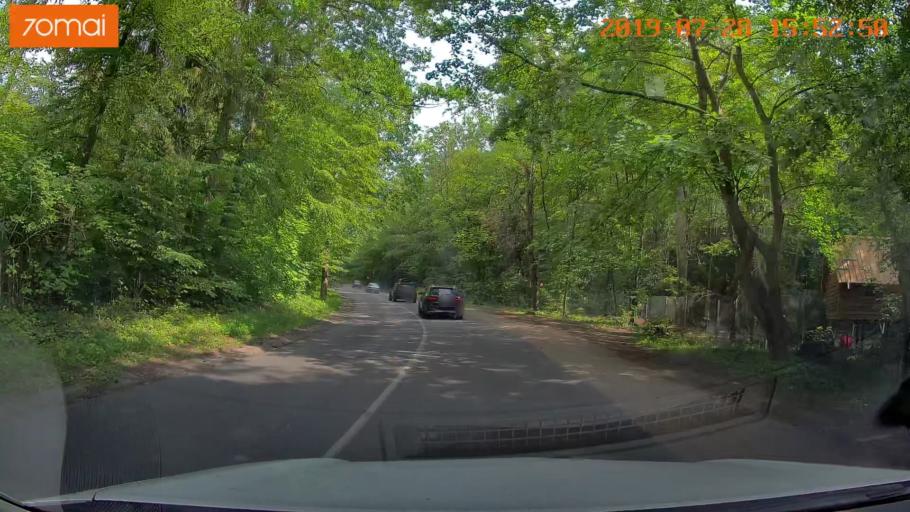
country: RU
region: Kaliningrad
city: Otradnoye
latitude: 54.9395
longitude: 20.1176
